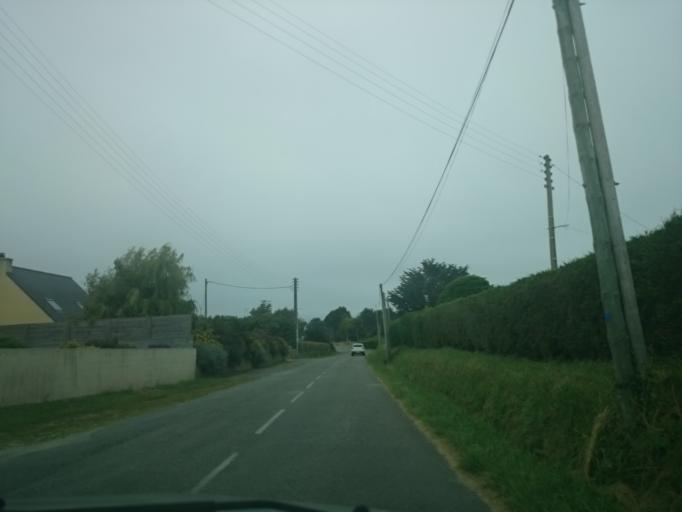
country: FR
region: Brittany
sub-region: Departement du Finistere
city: Saint-Pabu
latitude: 48.5693
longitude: -4.6243
